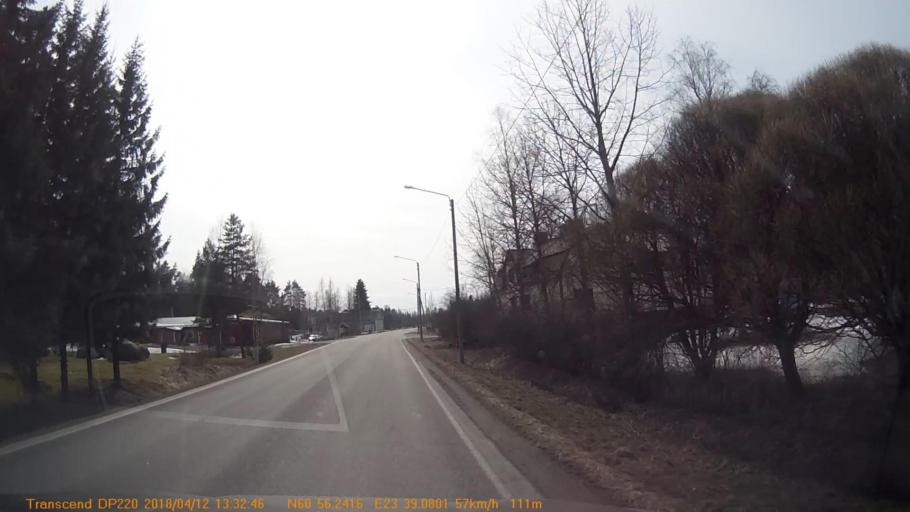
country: FI
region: Haeme
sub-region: Forssa
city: Forssa
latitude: 60.9372
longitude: 23.6512
